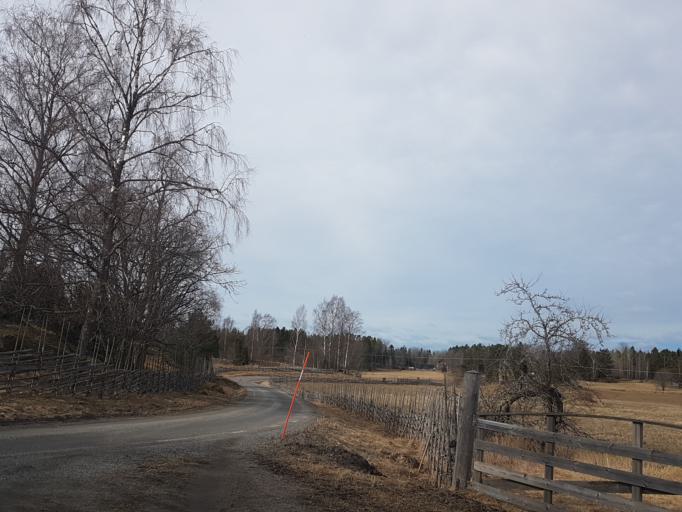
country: SE
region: Stockholm
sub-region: Norrtalje Kommun
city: Norrtalje
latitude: 59.6858
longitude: 18.6022
